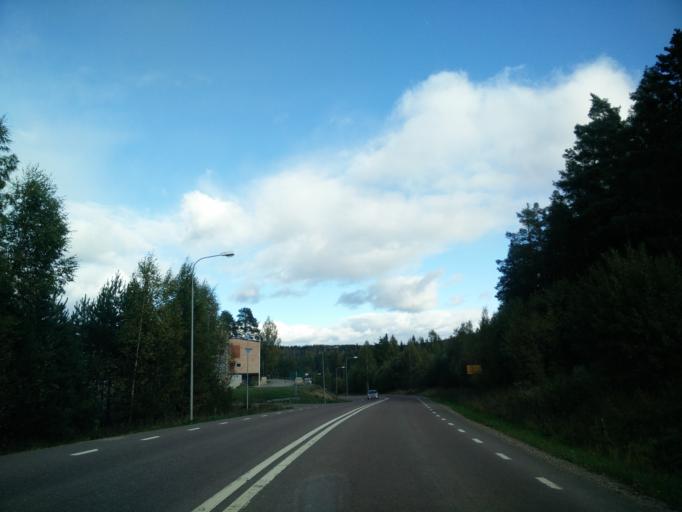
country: SE
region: Vaesternorrland
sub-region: Sundsvalls Kommun
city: Matfors
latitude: 62.3543
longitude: 17.0155
